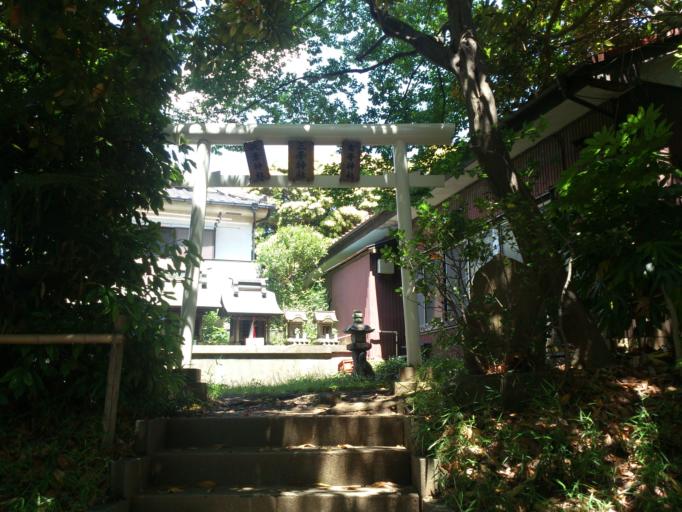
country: JP
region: Chiba
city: Chiba
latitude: 35.6484
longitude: 140.0667
